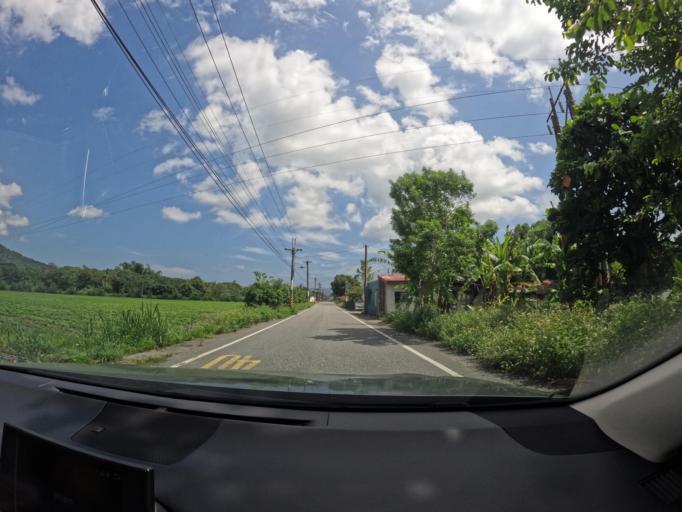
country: TW
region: Taiwan
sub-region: Hualien
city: Hualian
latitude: 23.7141
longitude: 121.4154
